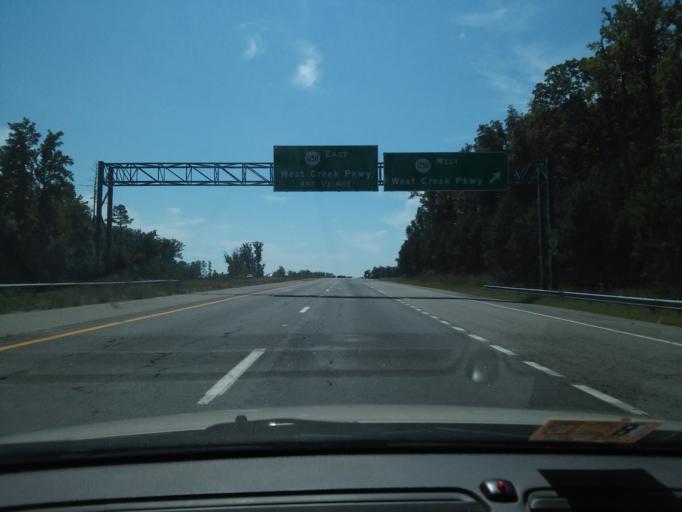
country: US
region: Virginia
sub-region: Henrico County
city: Short Pump
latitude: 37.6185
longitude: -77.6636
